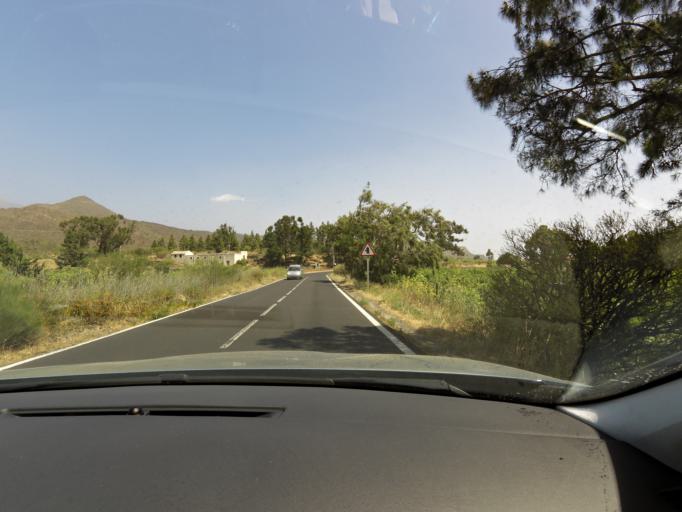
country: ES
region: Canary Islands
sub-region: Provincia de Santa Cruz de Tenerife
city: Santiago del Teide
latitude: 28.3014
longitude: -16.8154
